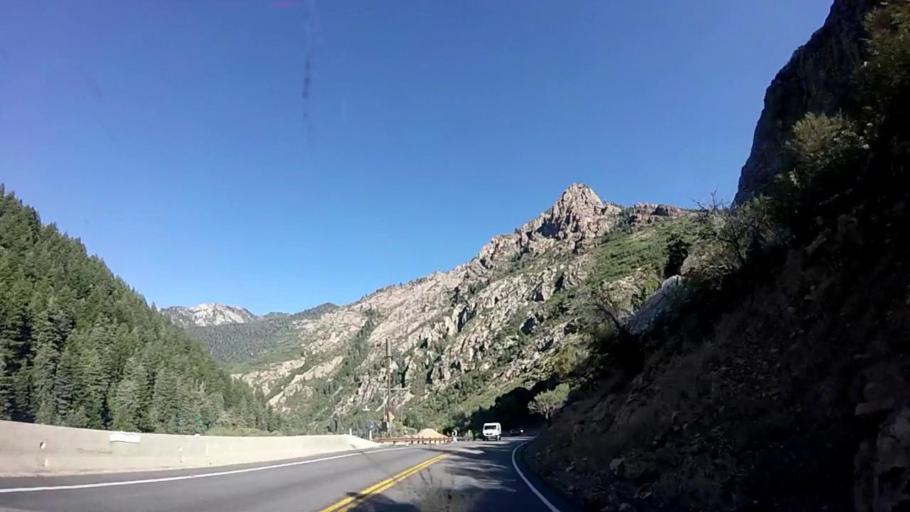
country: US
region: Utah
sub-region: Salt Lake County
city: Mount Olympus
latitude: 40.6332
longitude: -111.7223
